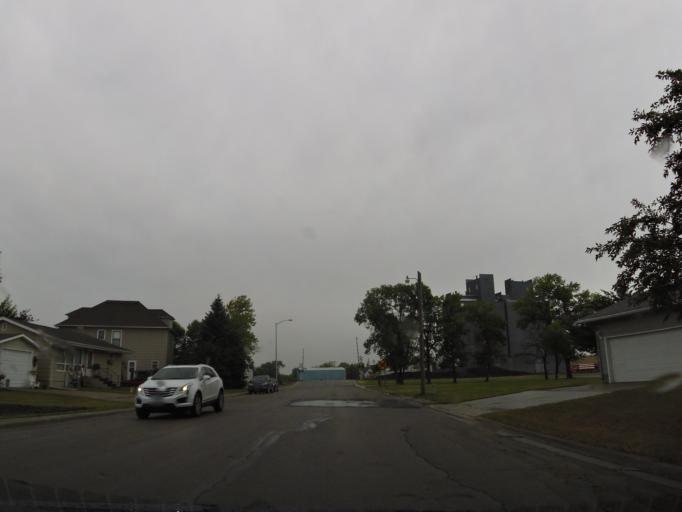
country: US
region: Minnesota
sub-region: Marshall County
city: Warren
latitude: 48.4491
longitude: -96.8714
